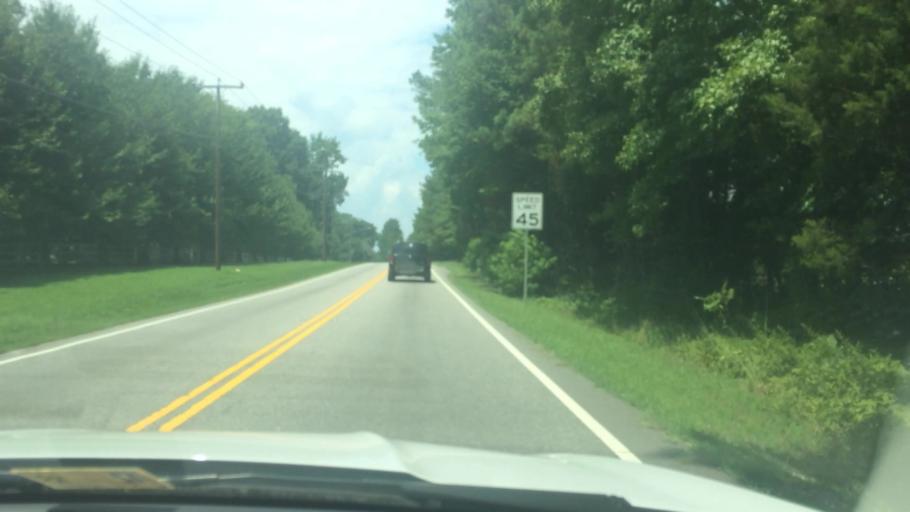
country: US
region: Virginia
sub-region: York County
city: Yorktown
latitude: 37.1993
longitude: -76.5773
